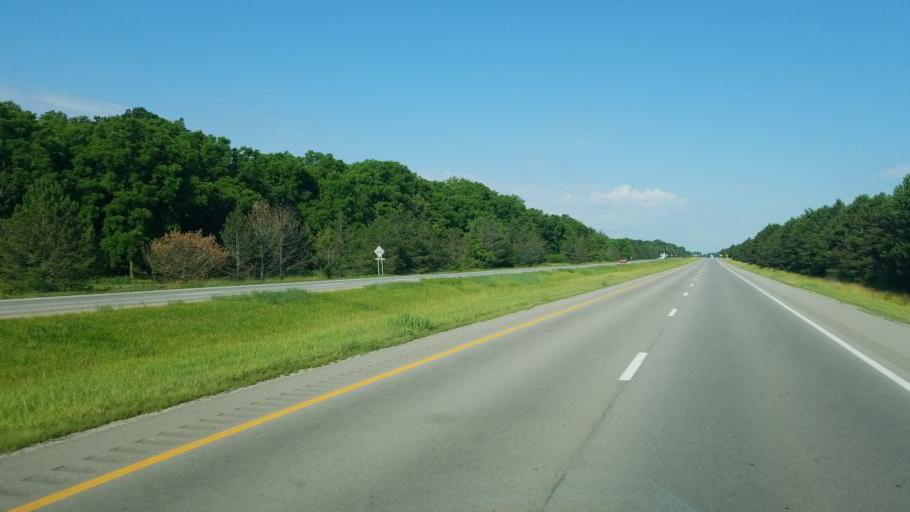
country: US
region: Ohio
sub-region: Wyandot County
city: Carey
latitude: 40.9820
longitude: -83.5053
